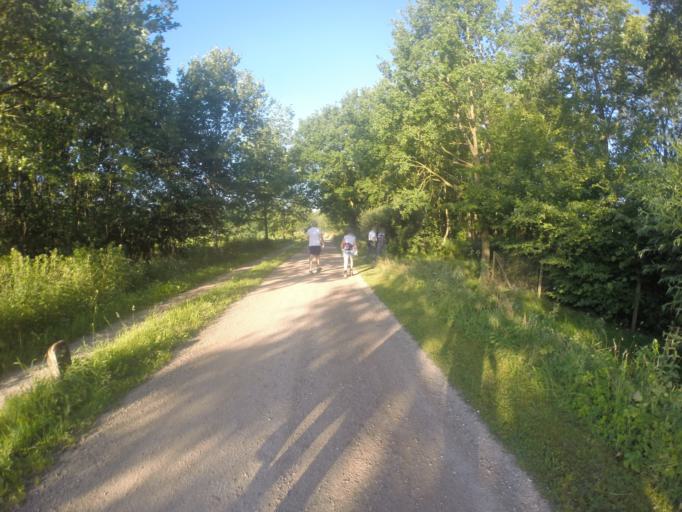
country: NL
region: Gelderland
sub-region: Gemeente Lochem
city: Barchem
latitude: 52.1170
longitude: 6.4297
